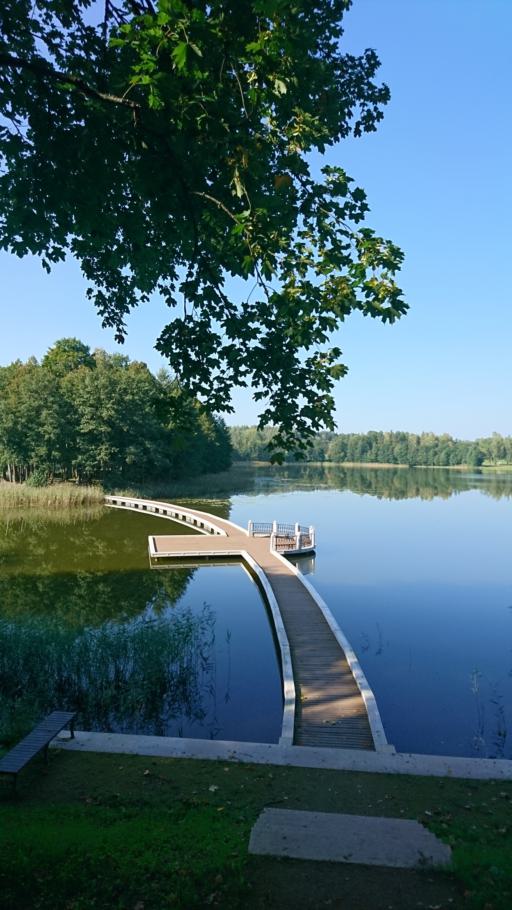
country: LT
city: Juodupe
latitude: 56.1612
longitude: 25.5237
